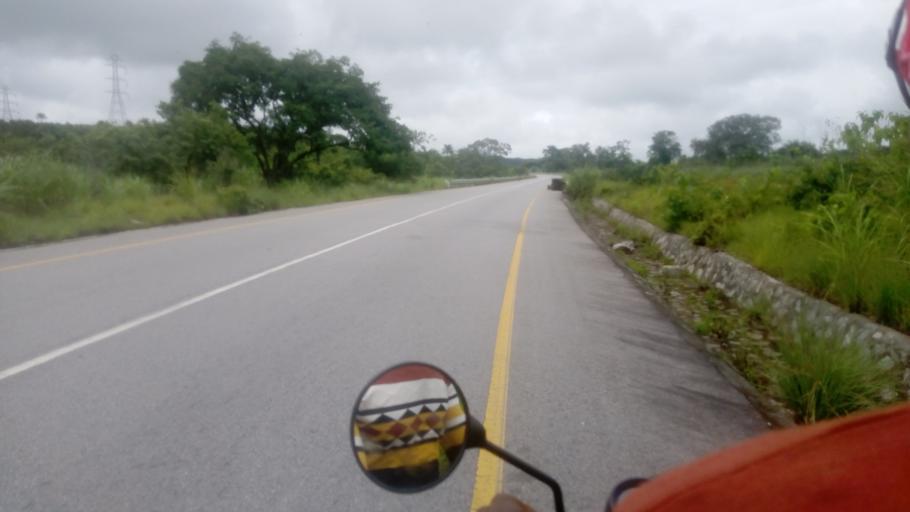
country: SL
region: Northern Province
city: Masaka
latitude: 8.6548
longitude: -11.7796
